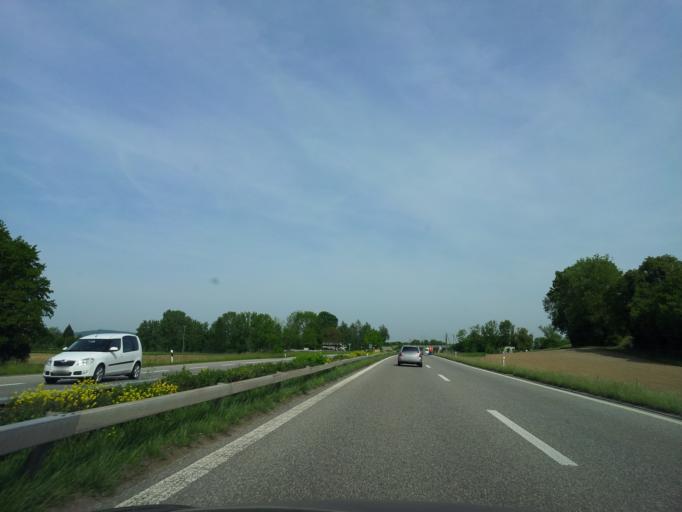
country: CH
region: Zurich
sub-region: Bezirk Buelach
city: Kloten / Freienberg (Chanzler-Chlini Chaseren)
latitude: 47.4721
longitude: 8.5580
